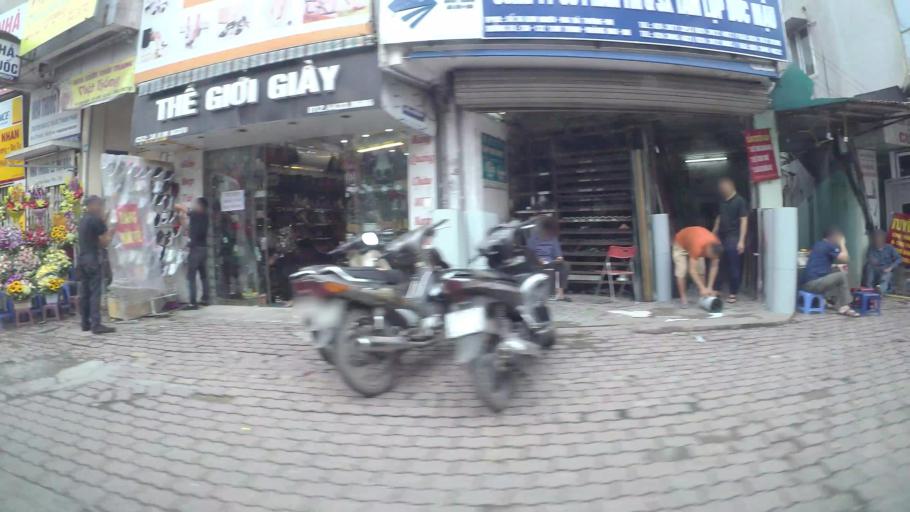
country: VN
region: Ha Noi
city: Hai BaTrung
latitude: 21.0081
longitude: 105.8607
